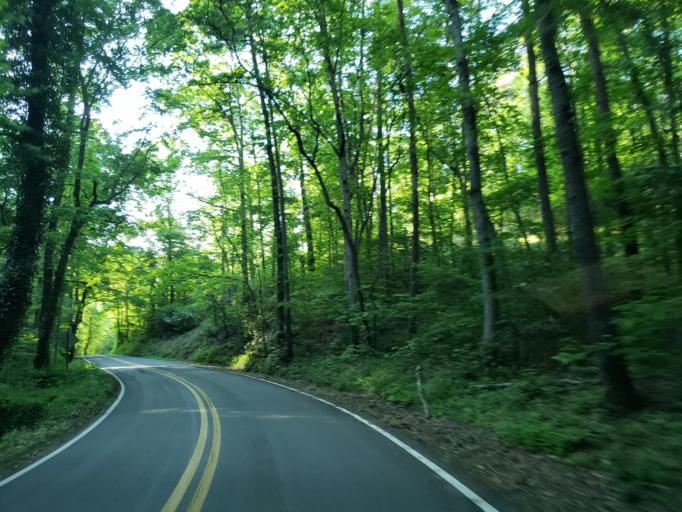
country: US
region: Georgia
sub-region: Murray County
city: Chatsworth
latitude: 34.6640
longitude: -84.6465
